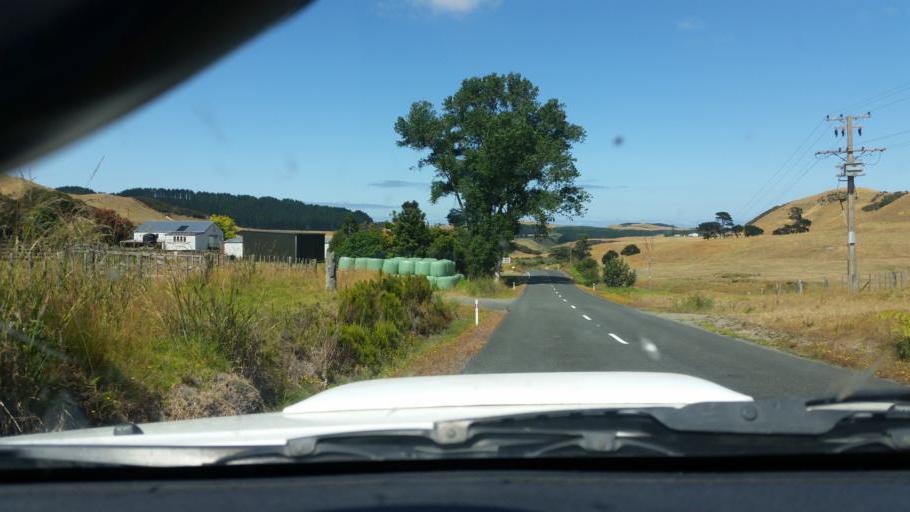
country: NZ
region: Northland
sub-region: Kaipara District
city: Dargaville
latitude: -35.8224
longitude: 173.6820
